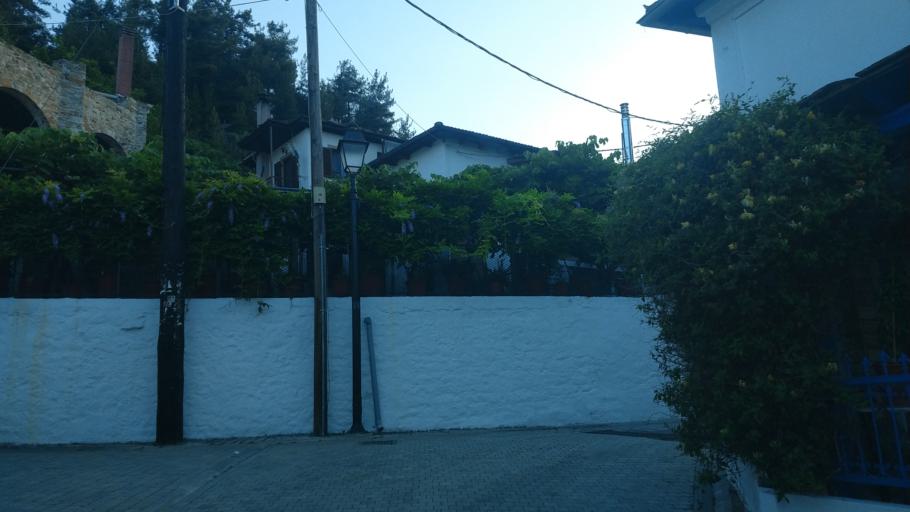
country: GR
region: East Macedonia and Thrace
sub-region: Nomos Kavalas
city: Potamia
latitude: 40.7303
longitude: 24.7274
